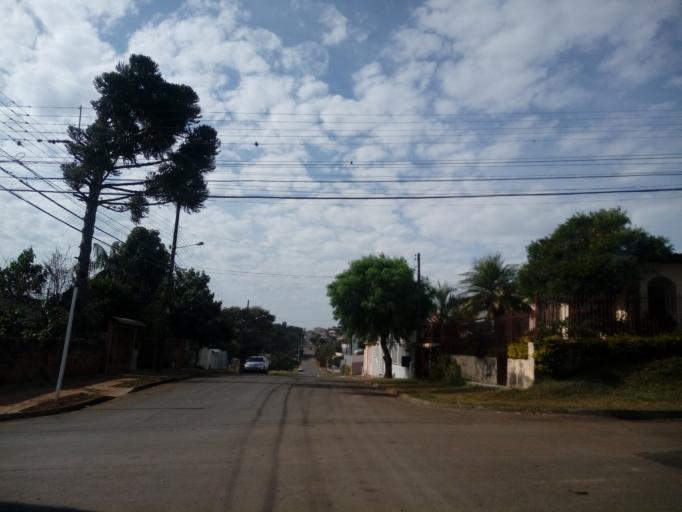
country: BR
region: Santa Catarina
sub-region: Chapeco
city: Chapeco
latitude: -27.1185
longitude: -52.6296
